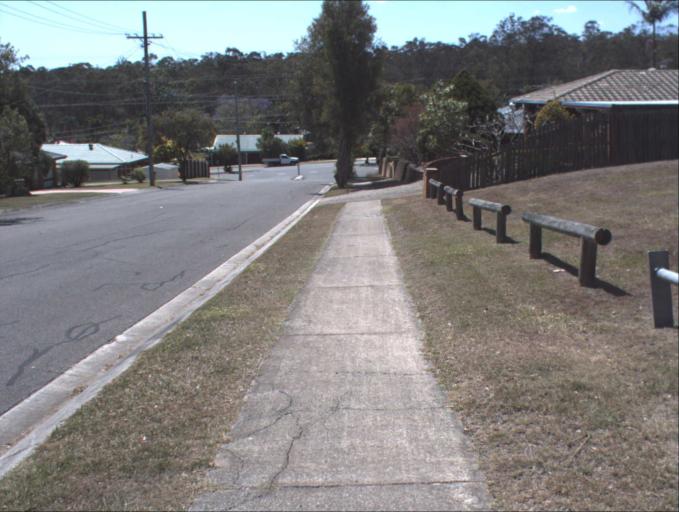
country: AU
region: Queensland
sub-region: Logan
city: Springwood
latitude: -27.6039
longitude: 153.1432
